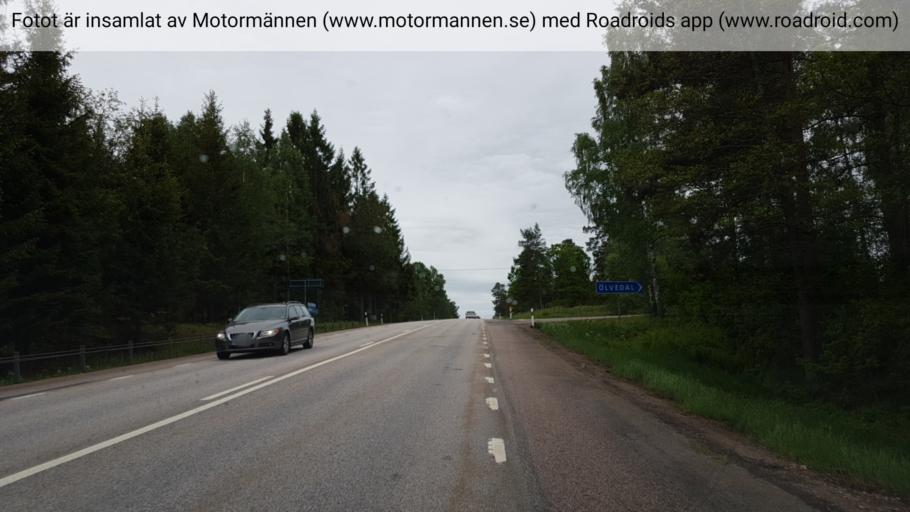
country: SE
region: Kalmar
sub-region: Oskarshamns Kommun
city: Oskarshamn
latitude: 57.4763
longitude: 16.5175
